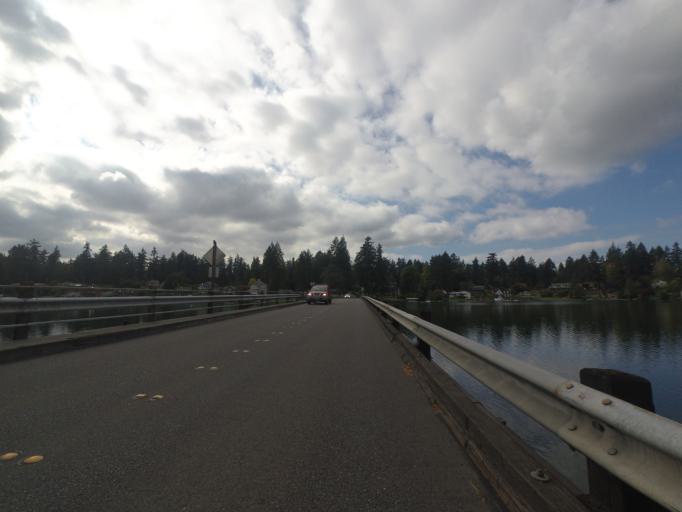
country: US
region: Washington
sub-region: Pierce County
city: Lakewood
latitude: 47.1666
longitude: -122.5398
